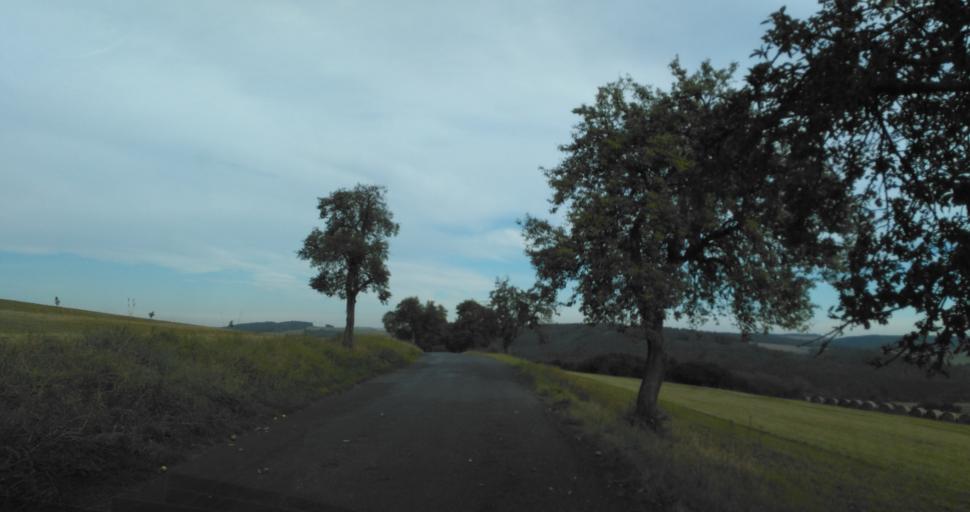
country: CZ
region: Plzensky
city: Zbiroh
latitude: 49.9569
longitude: 13.7742
